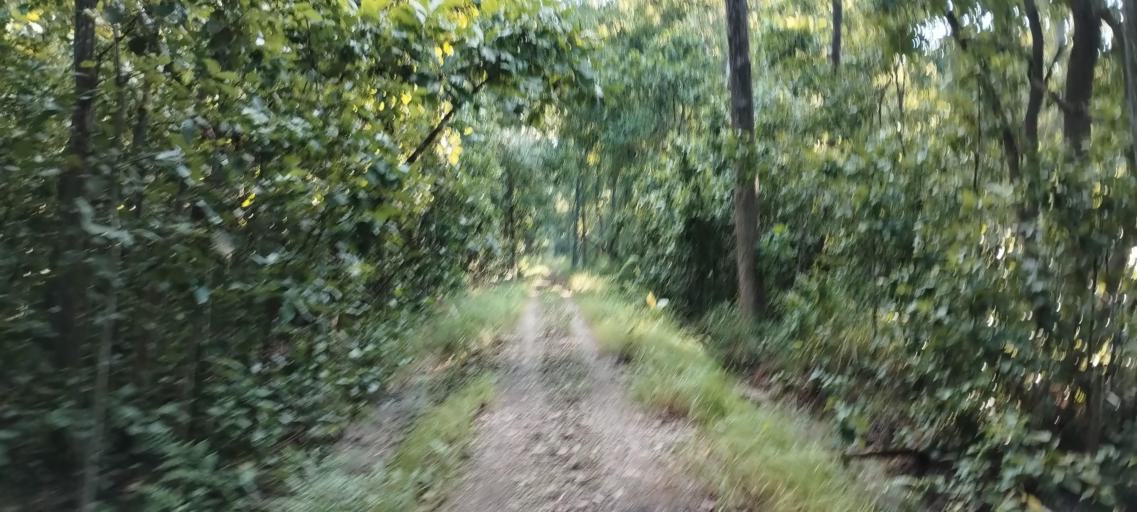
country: NP
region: Far Western
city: Tikapur
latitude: 28.5145
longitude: 81.2723
